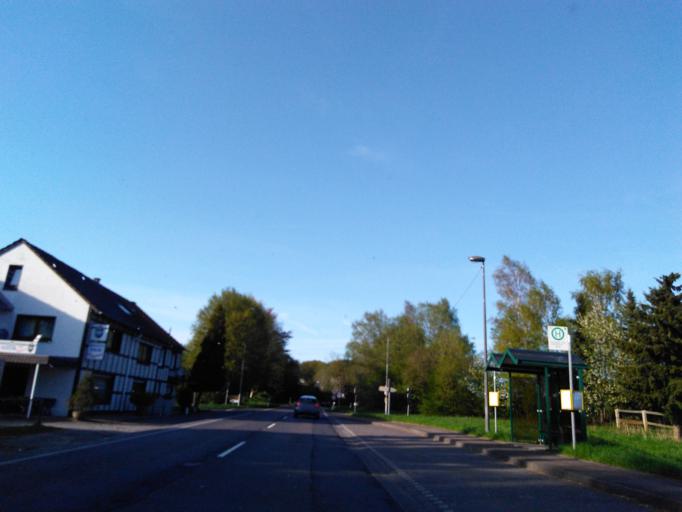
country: DE
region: North Rhine-Westphalia
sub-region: Regierungsbezirk Koln
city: Hennef
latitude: 50.8522
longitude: 7.2996
